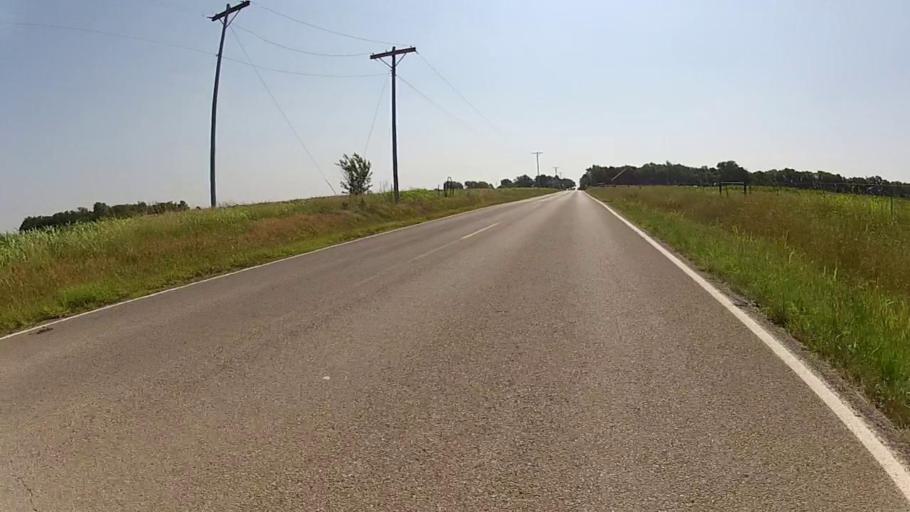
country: US
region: Kansas
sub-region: Montgomery County
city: Independence
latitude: 37.1929
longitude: -95.7458
